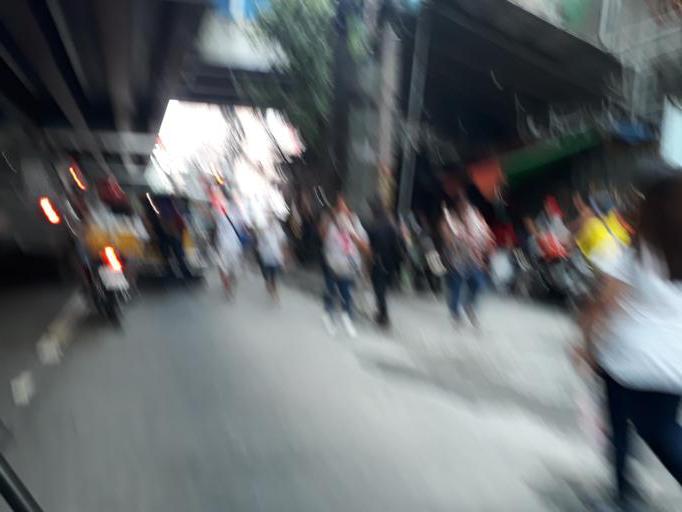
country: PH
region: Metro Manila
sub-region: City of Manila
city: Manila
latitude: 14.6163
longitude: 120.9829
